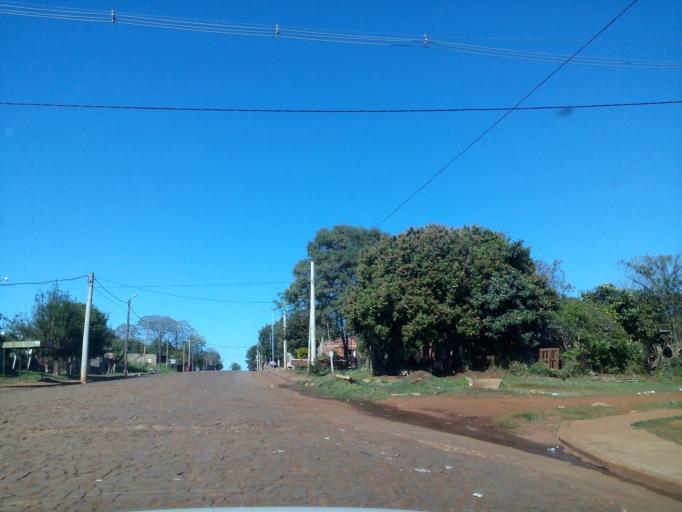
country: AR
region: Misiones
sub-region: Departamento de Capital
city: Posadas
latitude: -27.3787
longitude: -55.9485
